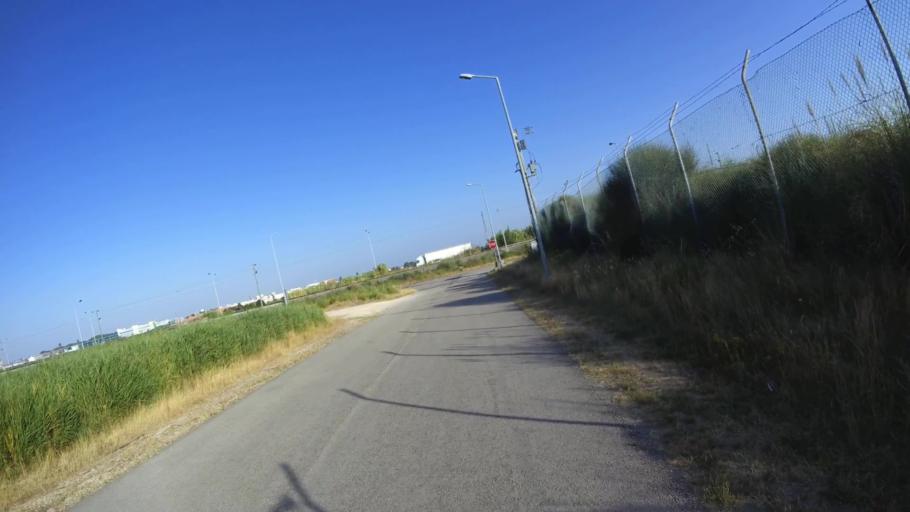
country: PT
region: Aveiro
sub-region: Aveiro
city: Aveiro
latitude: 40.6372
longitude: -8.6697
